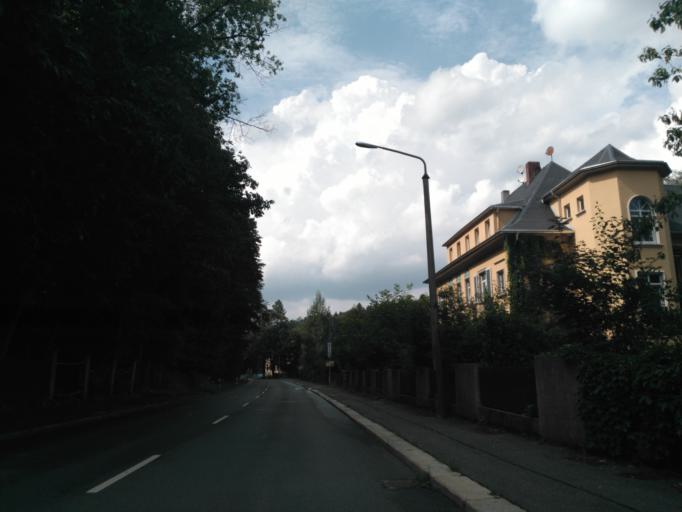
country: DE
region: Saxony
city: Rodewisch
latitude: 50.5320
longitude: 12.4365
